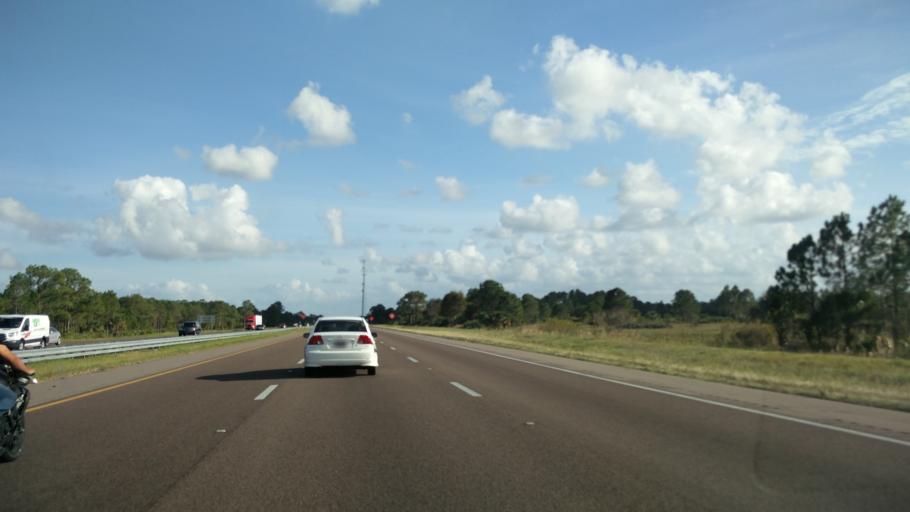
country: US
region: Florida
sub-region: Indian River County
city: Roseland
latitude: 27.8363
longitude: -80.5677
